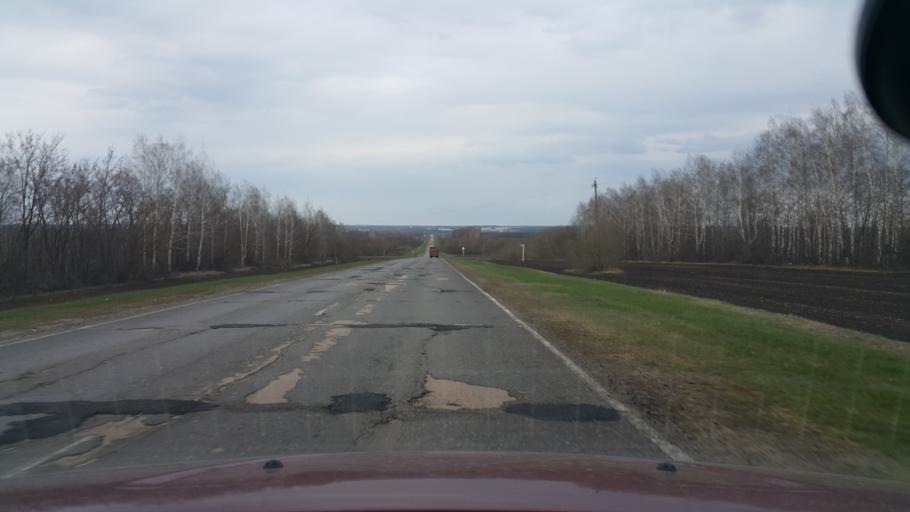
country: RU
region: Tambov
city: Bokino
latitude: 52.5729
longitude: 41.4202
